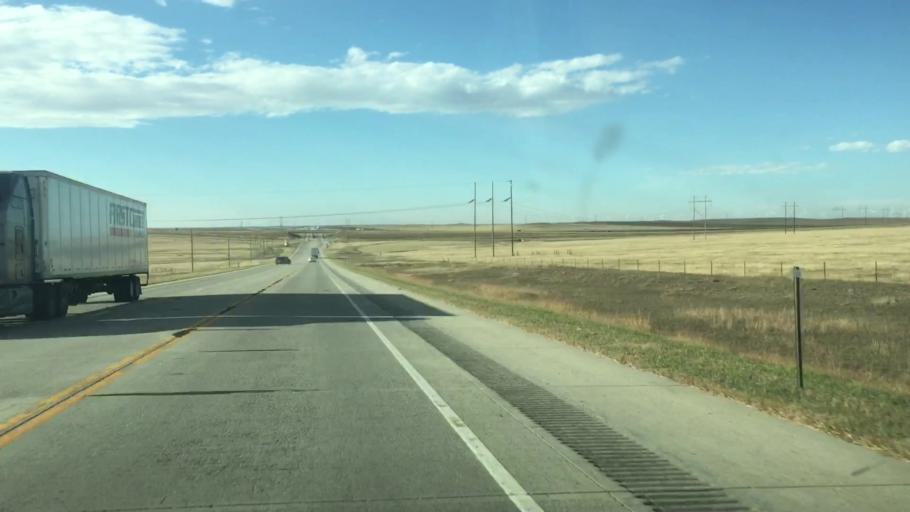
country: US
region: Colorado
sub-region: Lincoln County
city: Limon
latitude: 39.2545
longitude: -103.6384
